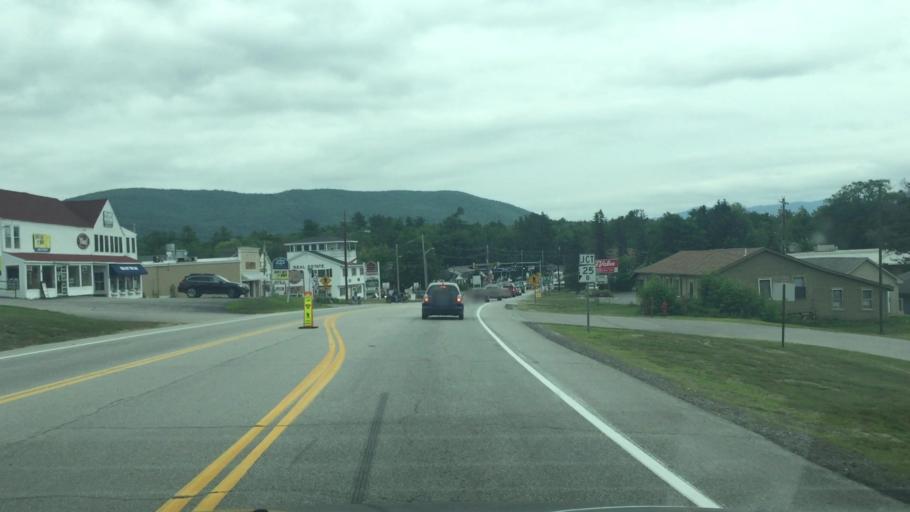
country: US
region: New Hampshire
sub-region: Carroll County
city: Center Harbor
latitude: 43.7082
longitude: -71.4622
